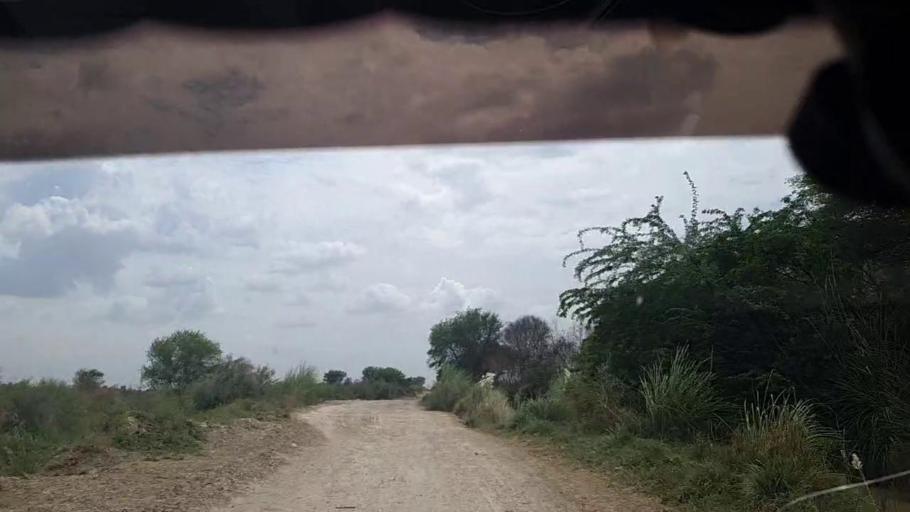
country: PK
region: Sindh
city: Rustam jo Goth
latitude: 28.0379
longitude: 68.9391
